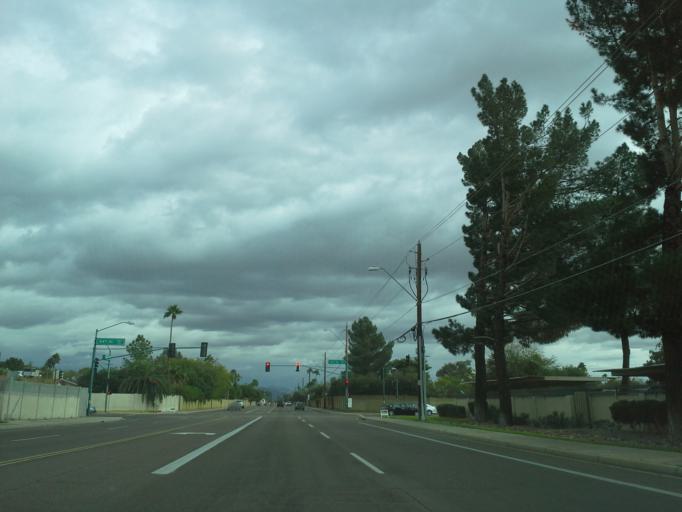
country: US
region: Arizona
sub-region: Maricopa County
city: Paradise Valley
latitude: 33.6117
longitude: -111.9875
